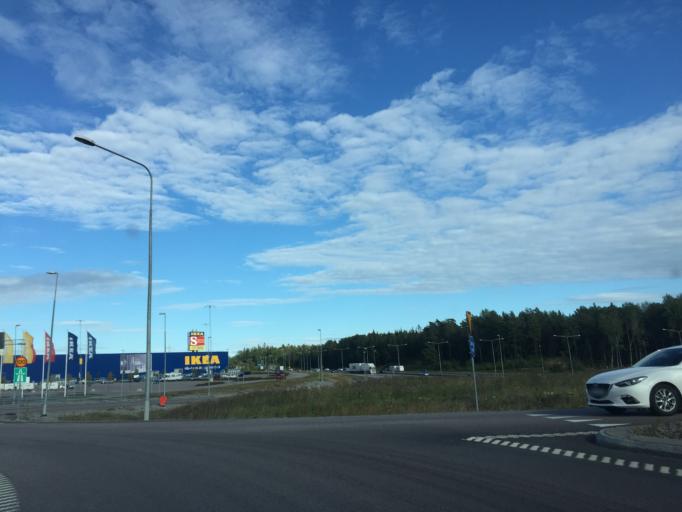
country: SE
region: Vaestmanland
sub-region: Vasteras
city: Vasteras
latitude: 59.6061
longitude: 16.4510
